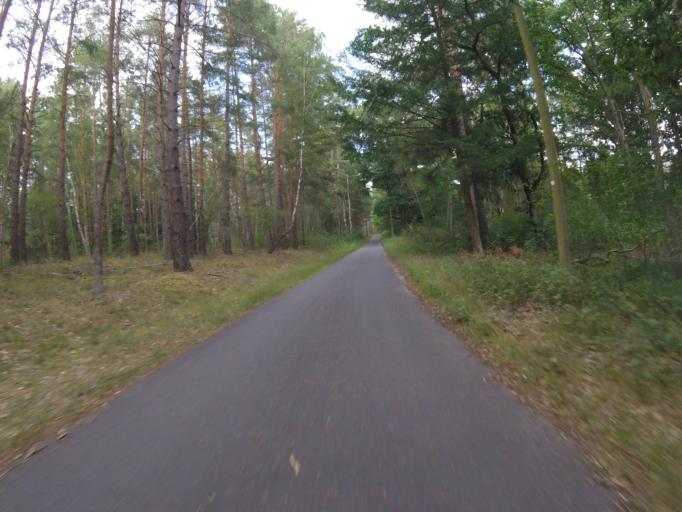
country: DE
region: Brandenburg
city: Halbe
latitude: 52.1615
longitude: 13.7594
